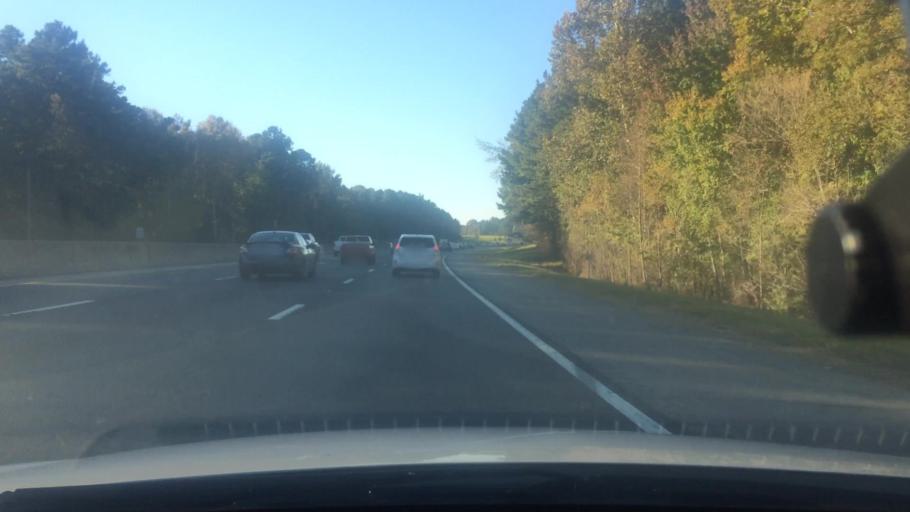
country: US
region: North Carolina
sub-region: Orange County
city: Chapel Hill
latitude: 35.9073
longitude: -78.9757
